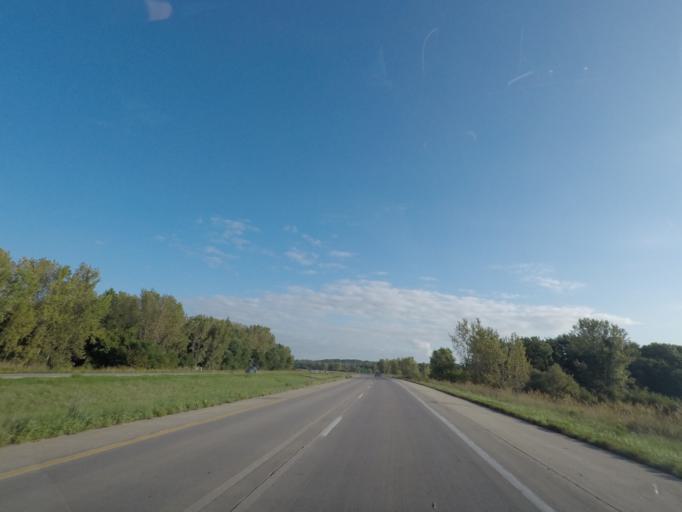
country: US
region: Iowa
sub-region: Polk County
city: Pleasant Hill
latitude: 41.5525
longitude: -93.5112
